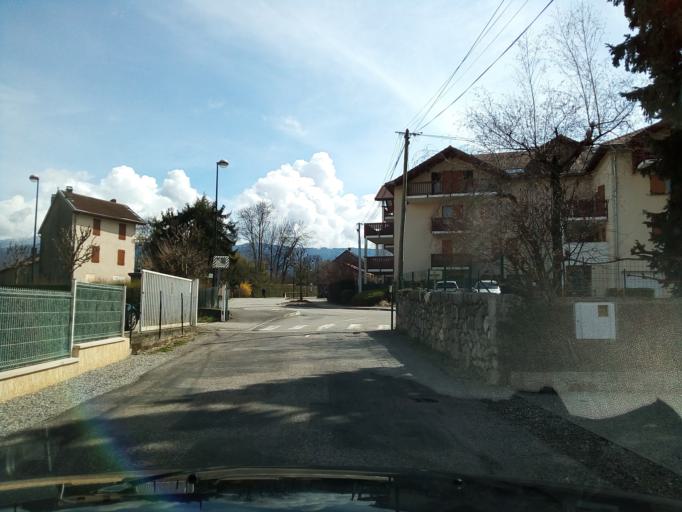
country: FR
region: Rhone-Alpes
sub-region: Departement de l'Isere
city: Chapareillan
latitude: 45.4687
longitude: 5.9890
